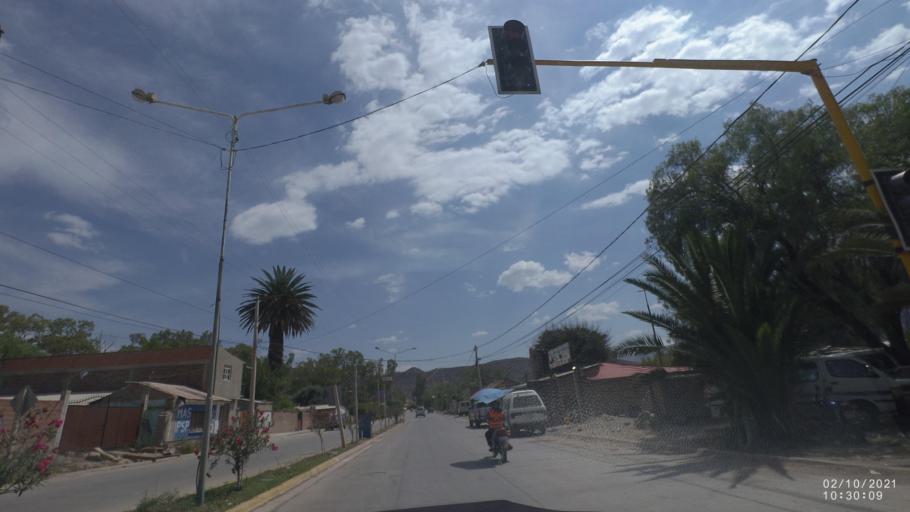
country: BO
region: Cochabamba
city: Capinota
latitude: -17.6990
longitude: -66.2655
